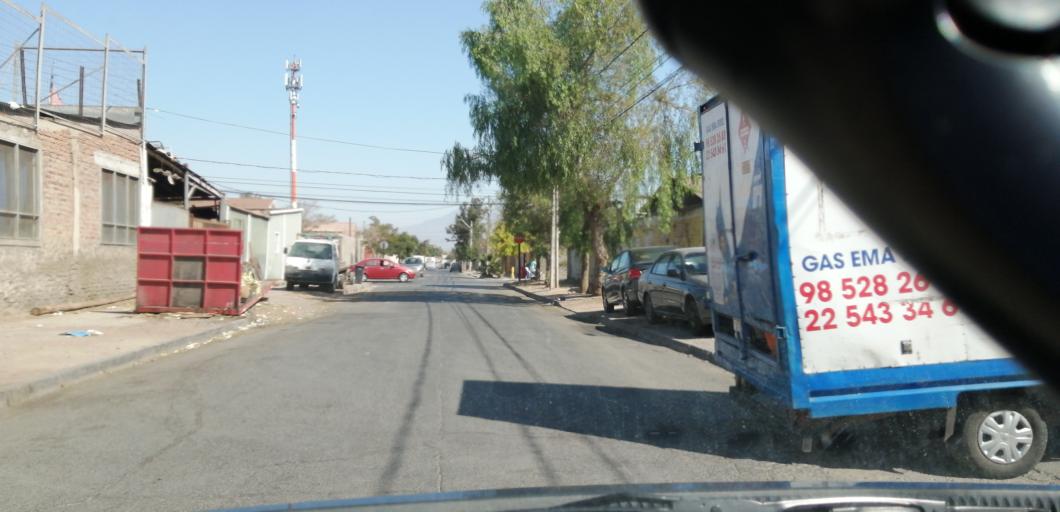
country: CL
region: Santiago Metropolitan
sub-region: Provincia de Santiago
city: Lo Prado
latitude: -33.4437
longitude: -70.7507
